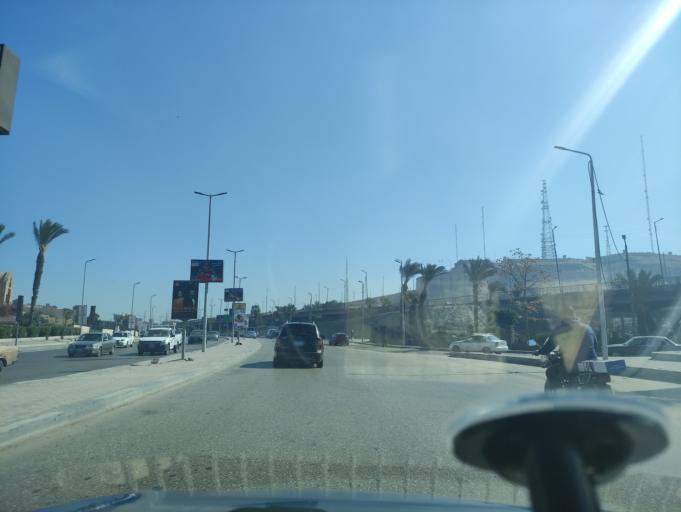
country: EG
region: Muhafazat al Qahirah
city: Cairo
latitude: 30.0248
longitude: 31.2608
